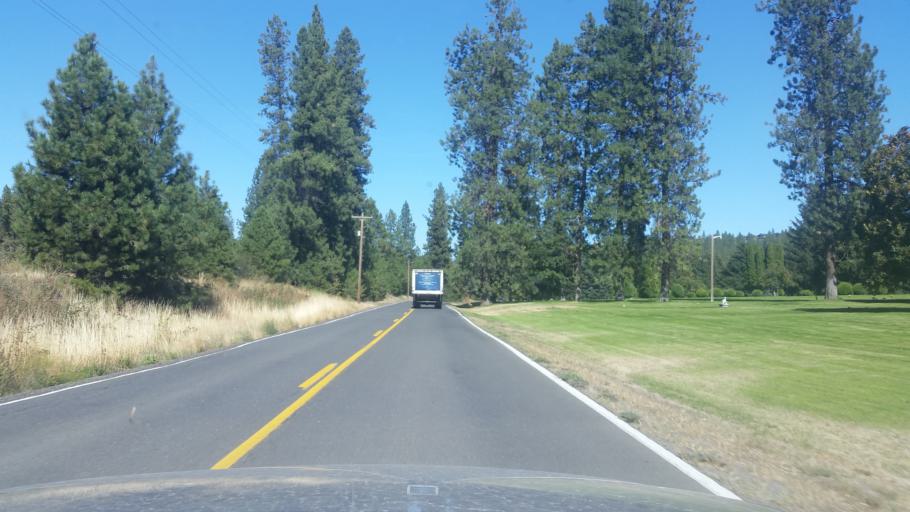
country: US
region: Washington
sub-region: Spokane County
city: Spokane
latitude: 47.5975
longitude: -117.4440
